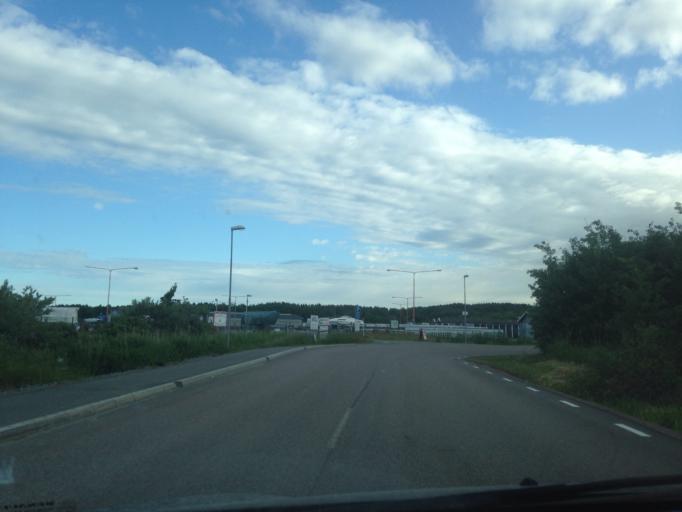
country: SE
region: Vaestra Goetaland
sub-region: Goteborg
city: Torslanda
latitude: 57.7627
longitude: 11.8088
